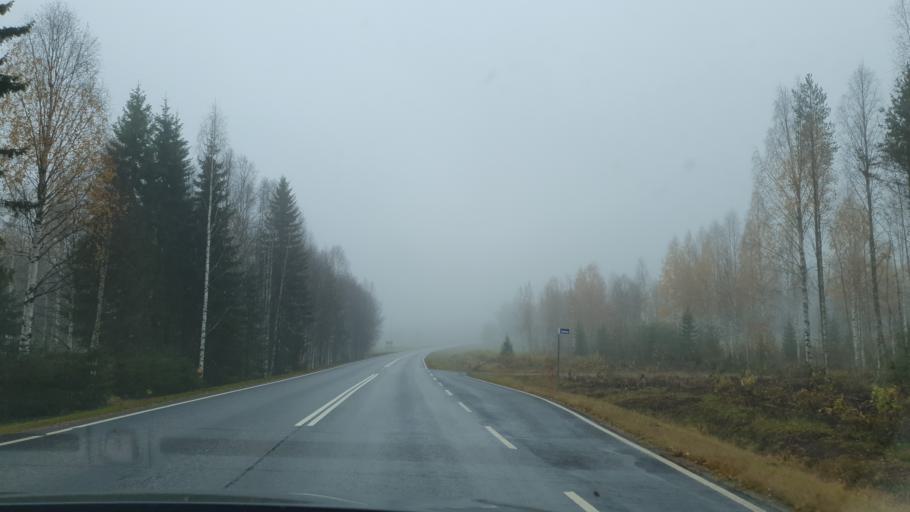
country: FI
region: Lapland
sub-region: Rovaniemi
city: Rovaniemi
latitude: 66.8092
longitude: 25.4091
